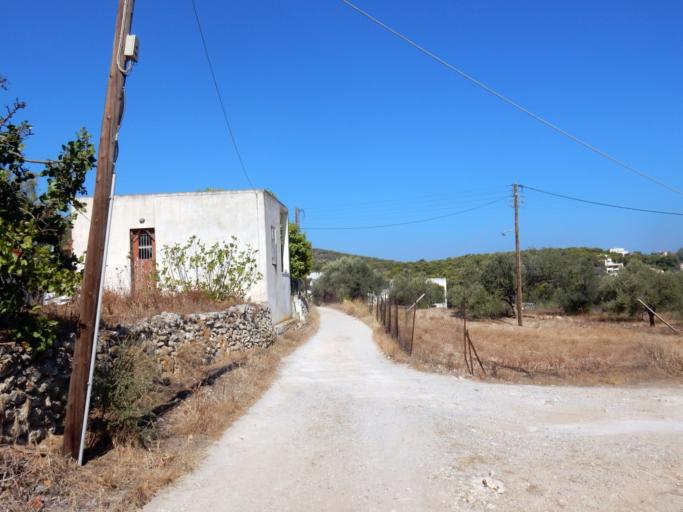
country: GR
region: Attica
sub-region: Nomos Piraios
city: Vathi
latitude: 37.7648
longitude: 23.5360
